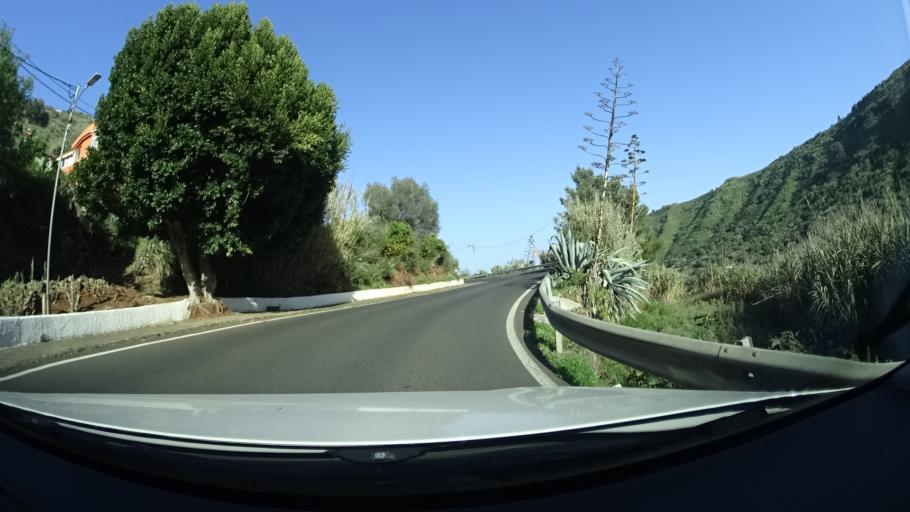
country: ES
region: Canary Islands
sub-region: Provincia de Las Palmas
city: Vega de San Mateo
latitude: 28.0191
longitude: -15.5538
